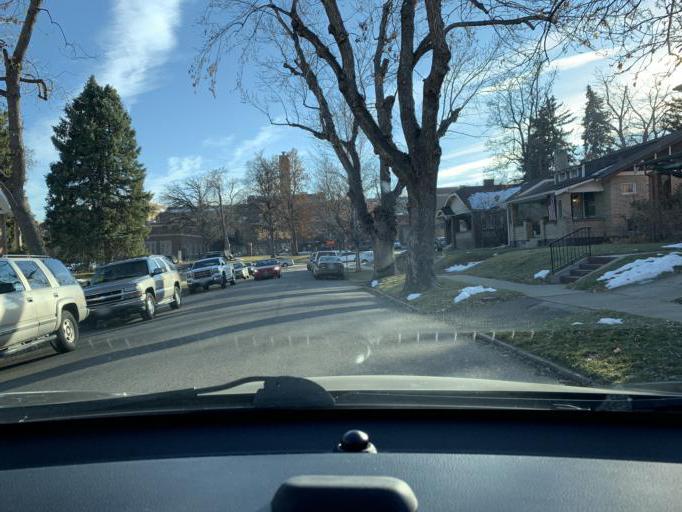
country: US
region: Colorado
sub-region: Adams County
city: Berkley
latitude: 39.7737
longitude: -105.0323
